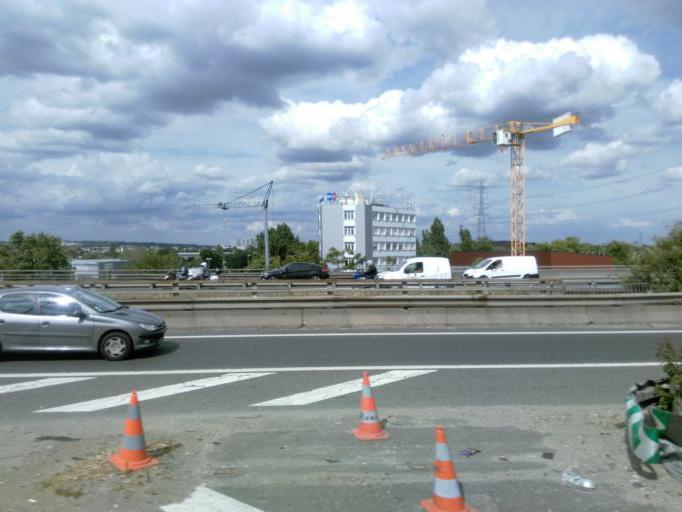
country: FR
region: Ile-de-France
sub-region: Departement des Hauts-de-Seine
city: Gennevilliers
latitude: 48.9402
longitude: 2.2932
